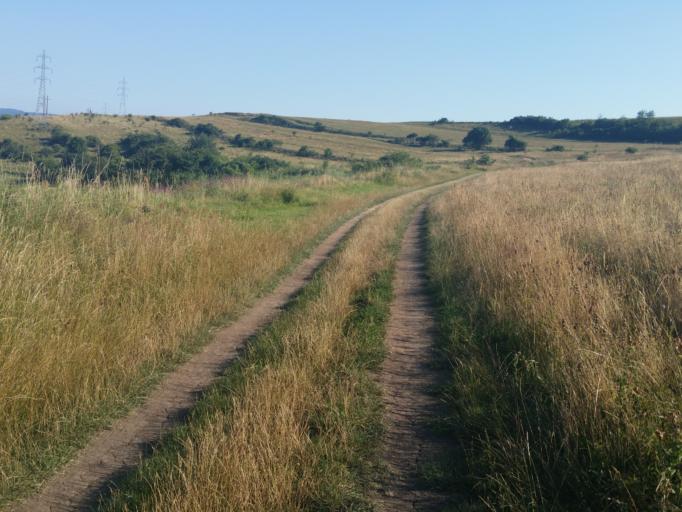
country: RO
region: Cluj
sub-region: Comuna Baciu
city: Baciu
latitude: 46.7999
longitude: 23.5290
